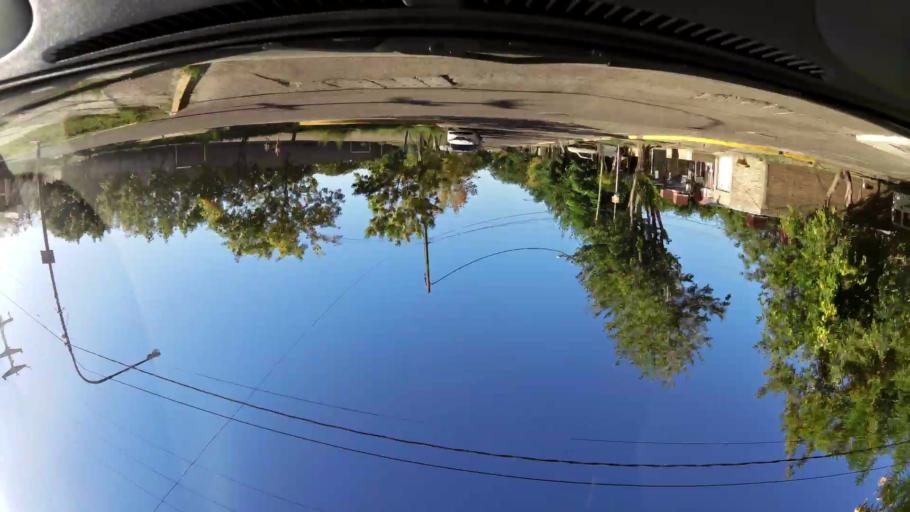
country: AR
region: Mendoza
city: Las Heras
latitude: -32.8445
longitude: -68.8254
